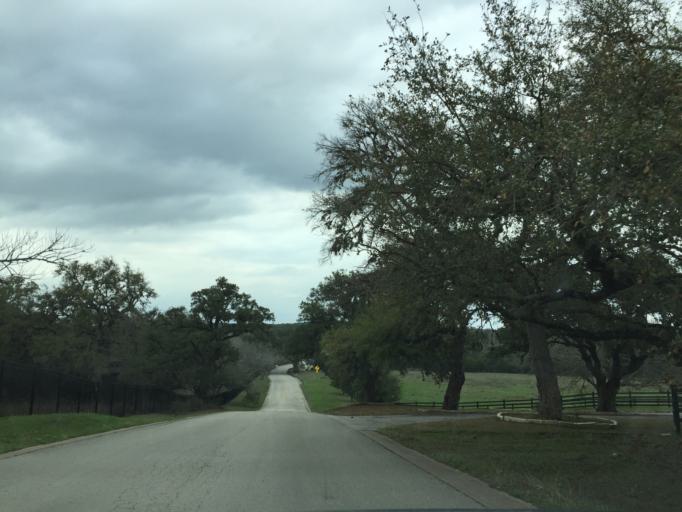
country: US
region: Texas
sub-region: Travis County
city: Shady Hollow
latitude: 30.1494
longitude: -97.9722
